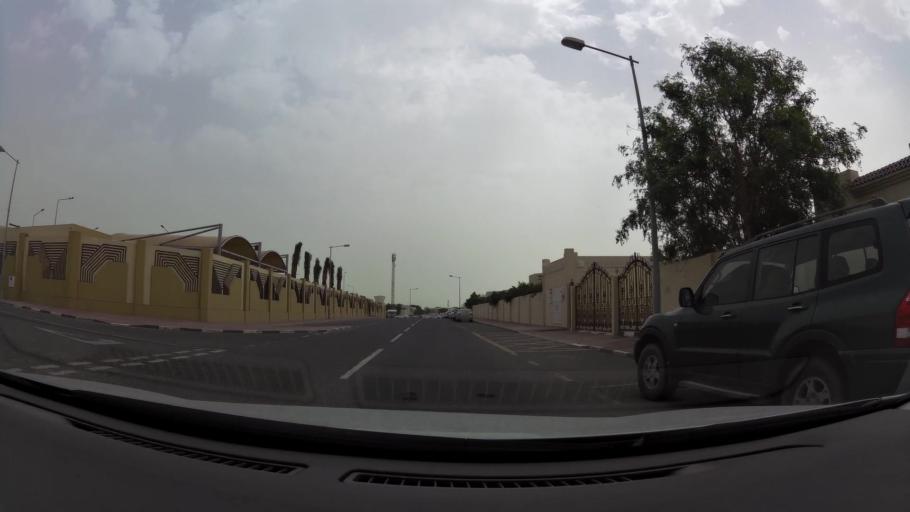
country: QA
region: Baladiyat ad Dawhah
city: Doha
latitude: 25.2564
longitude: 51.5263
